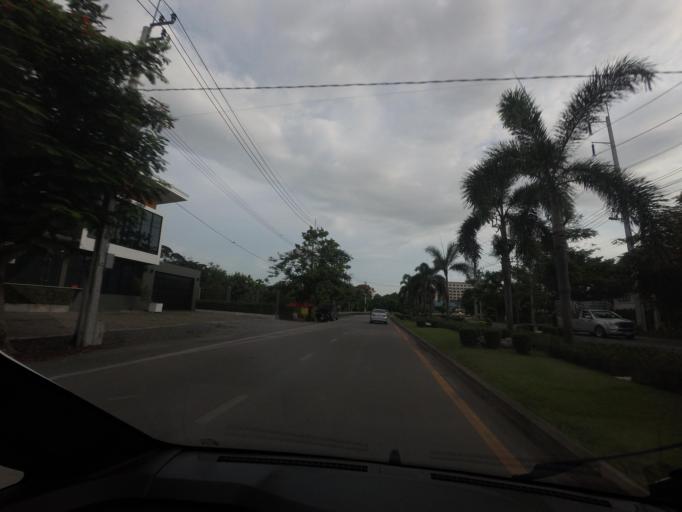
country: TH
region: Bangkok
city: Nong Chok
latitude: 13.8600
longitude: 100.8606
